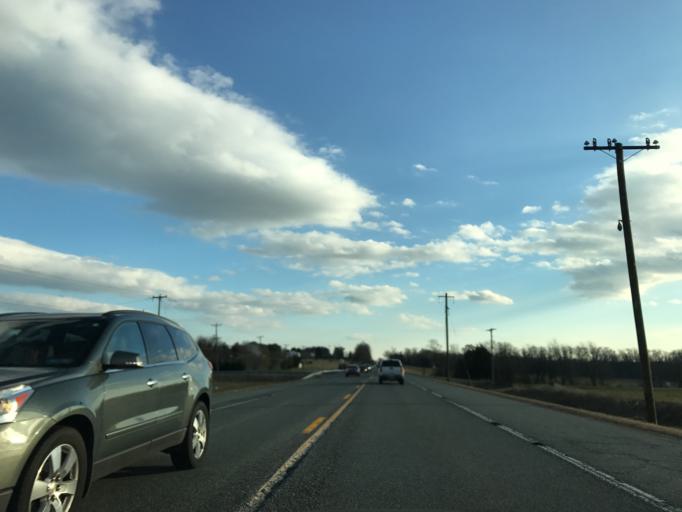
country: US
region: Maryland
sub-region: Cecil County
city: North East
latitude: 39.6635
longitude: -75.9558
